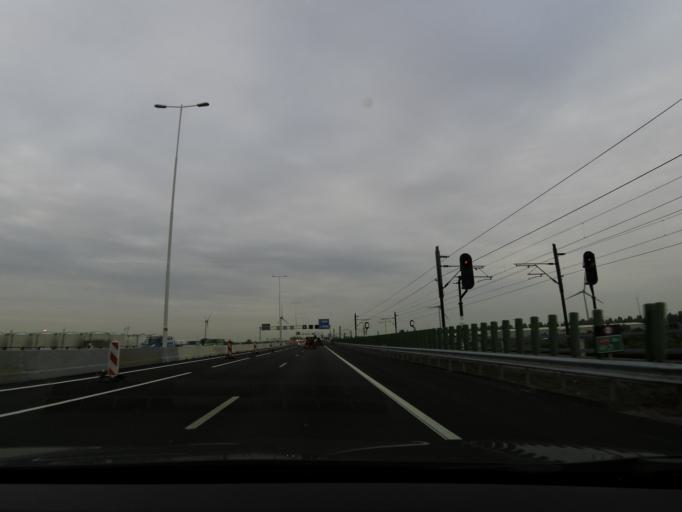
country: NL
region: South Holland
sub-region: Gemeente Maassluis
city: Maassluis
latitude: 51.8772
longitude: 4.2625
